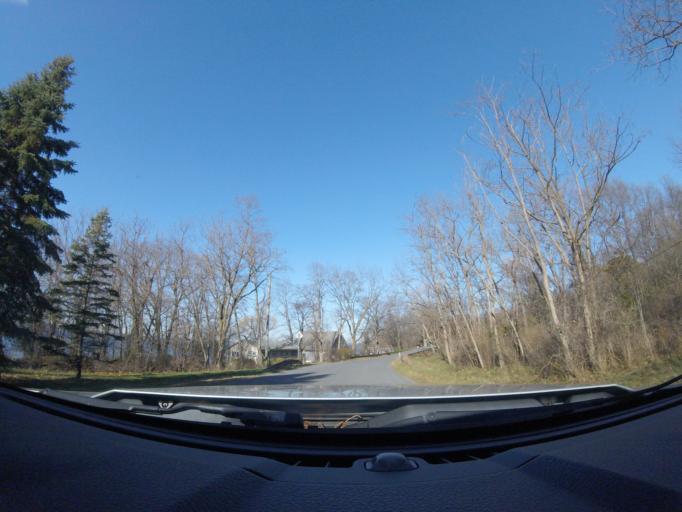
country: US
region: New York
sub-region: Cayuga County
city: Union Springs
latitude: 42.7179
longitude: -76.7077
